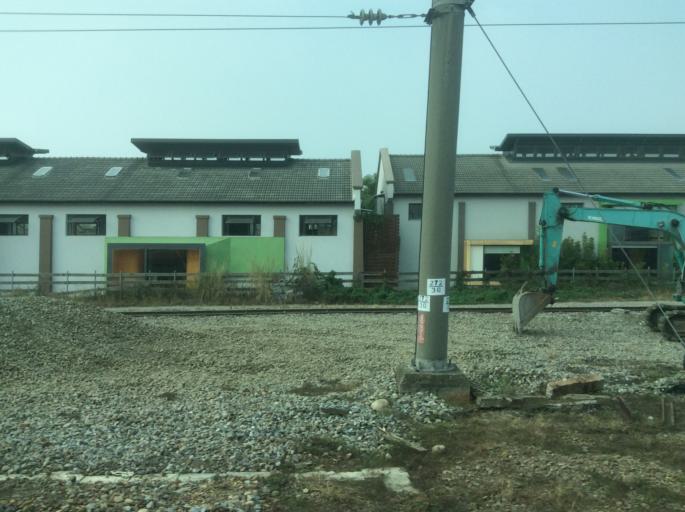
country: TW
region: Taiwan
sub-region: Yunlin
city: Douliu
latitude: 23.6746
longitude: 120.4823
